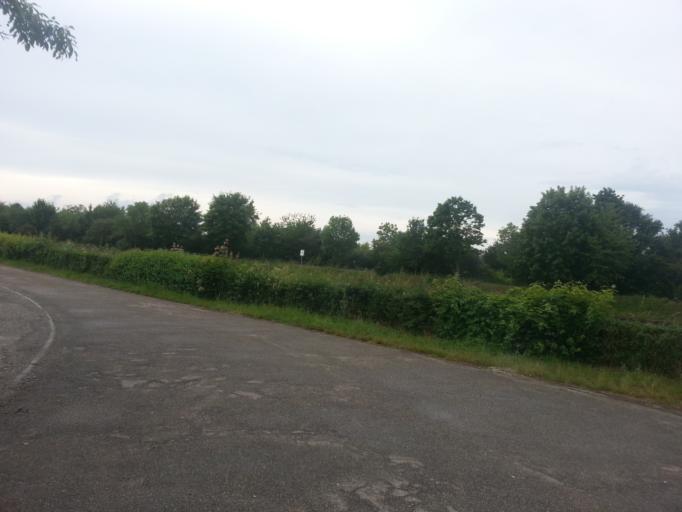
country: DE
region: Baden-Wuerttemberg
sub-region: Karlsruhe Region
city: Ilvesheim
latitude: 49.4783
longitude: 8.5345
